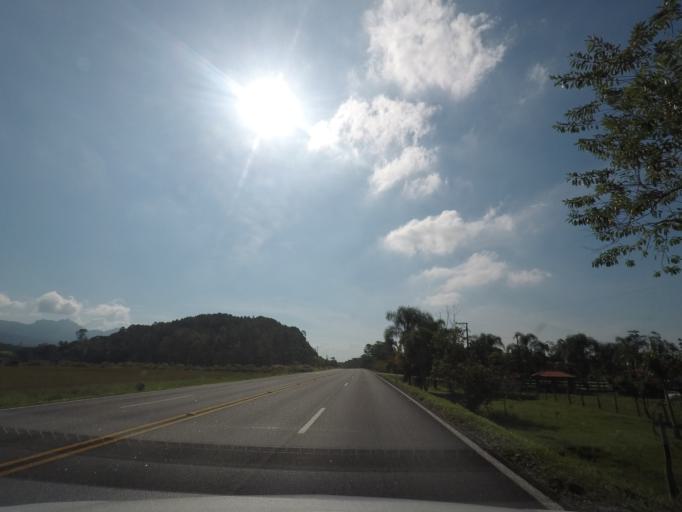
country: BR
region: Parana
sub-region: Pontal Do Parana
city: Pontal do Parana
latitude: -25.6312
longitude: -48.5949
